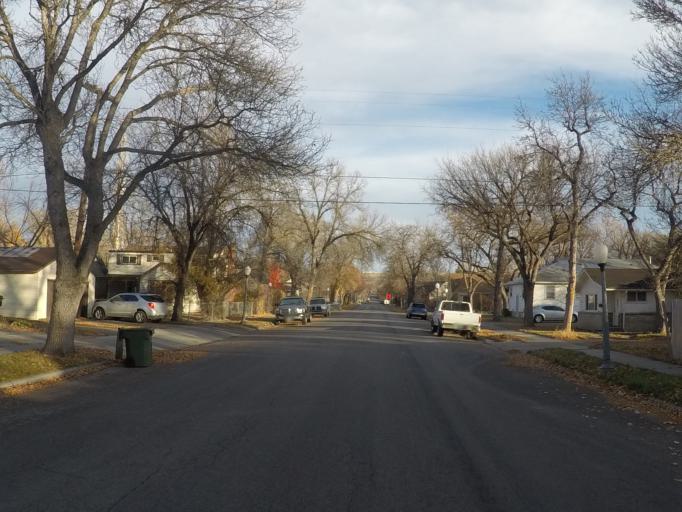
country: US
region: Montana
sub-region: Yellowstone County
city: Billings
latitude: 45.7793
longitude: -108.5305
